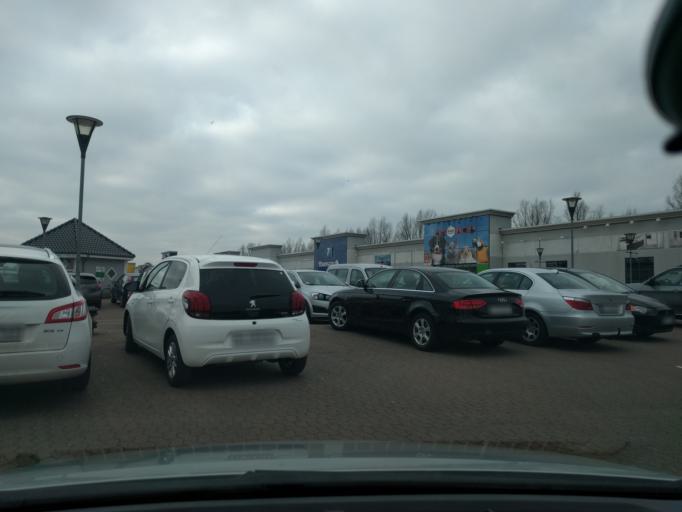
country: DK
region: Zealand
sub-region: Guldborgsund Kommune
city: Nykobing Falster
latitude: 54.7596
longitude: 11.8544
